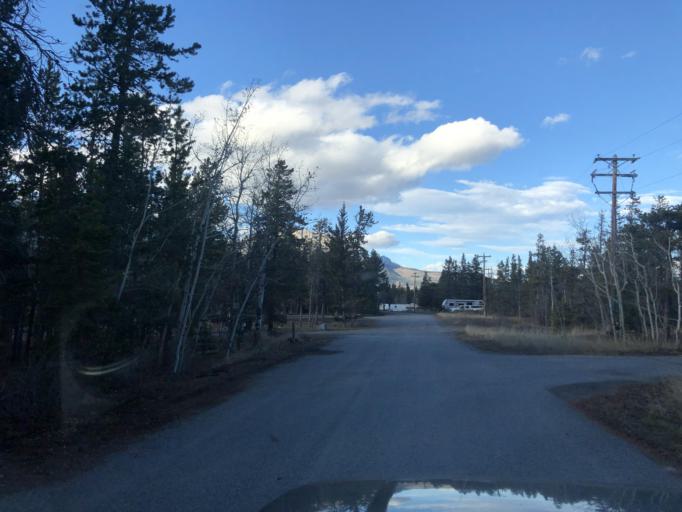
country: CA
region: Alberta
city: Canmore
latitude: 51.0715
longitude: -115.0800
